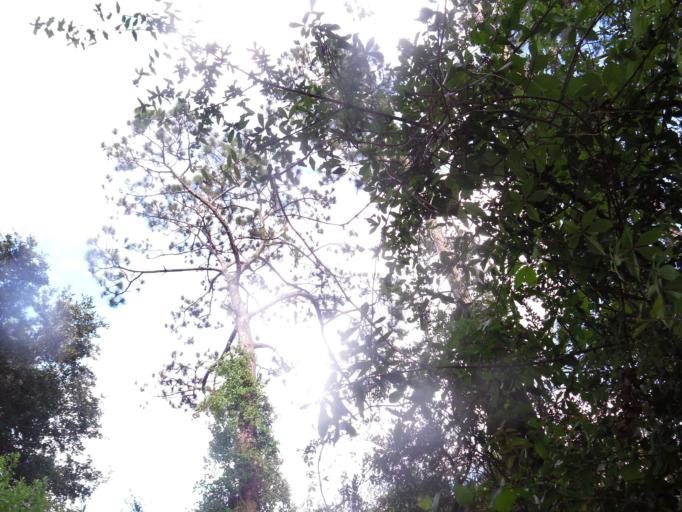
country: US
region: Florida
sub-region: Saint Johns County
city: Villano Beach
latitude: 30.0259
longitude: -81.3393
